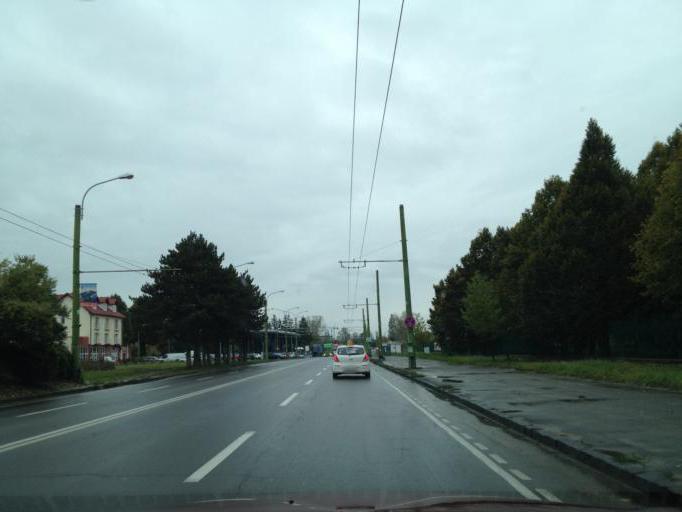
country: RO
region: Brasov
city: Brasov
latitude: 45.6801
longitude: 25.6146
